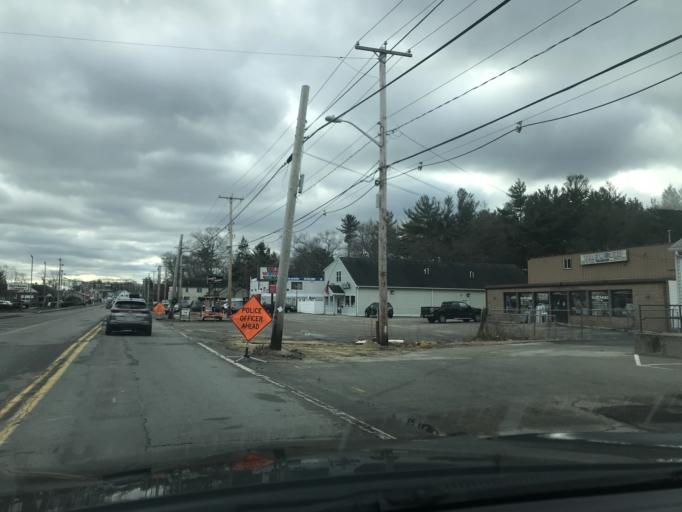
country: US
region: Massachusetts
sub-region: Plymouth County
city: Rockland
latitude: 42.1502
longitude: -70.9552
